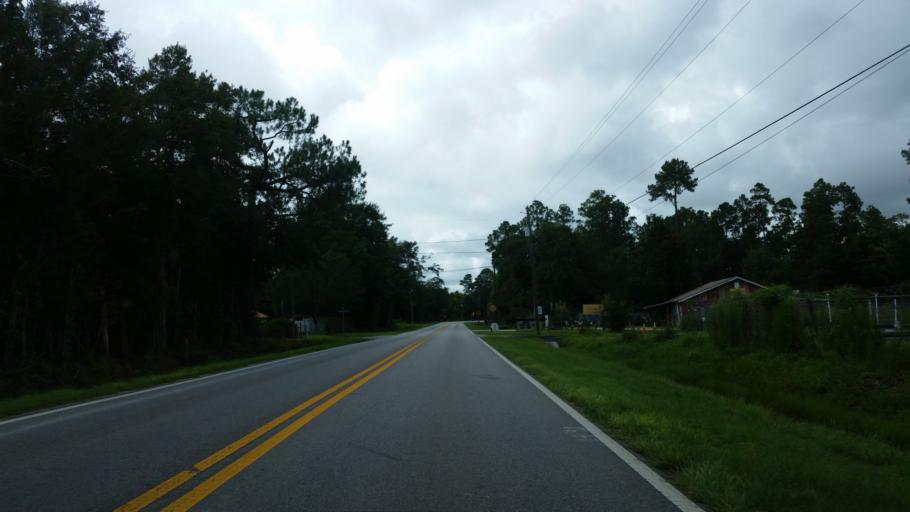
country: US
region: Florida
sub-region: Santa Rosa County
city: East Milton
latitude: 30.6086
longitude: -87.0192
